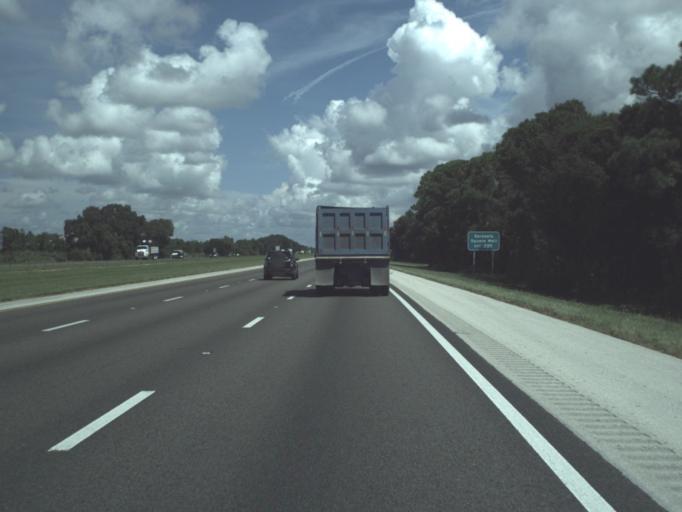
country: US
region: Florida
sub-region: Sarasota County
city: Lake Sarasota
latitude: 27.2538
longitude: -82.4490
